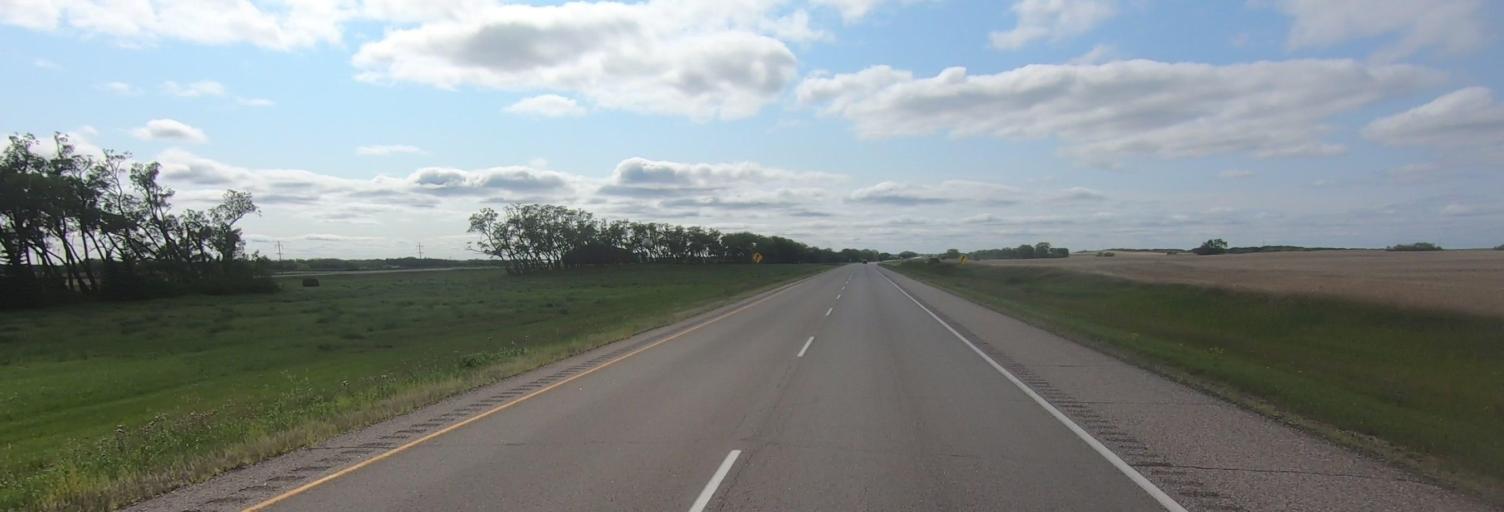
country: CA
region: Manitoba
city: Souris
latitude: 49.7700
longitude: -100.5233
